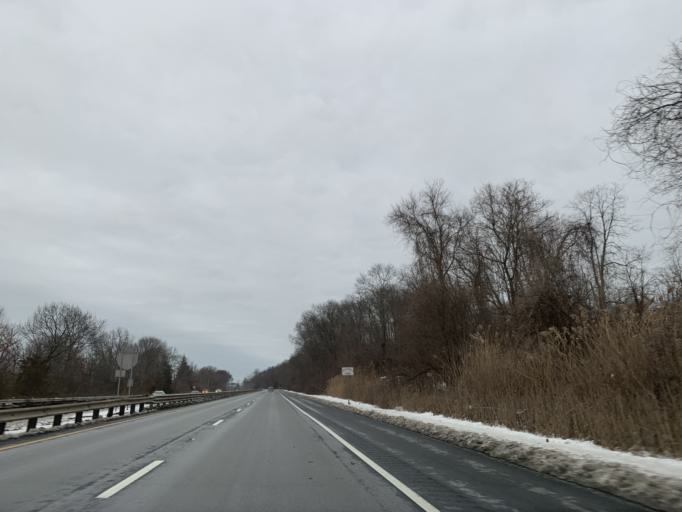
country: US
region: Massachusetts
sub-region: Bristol County
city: Somerset
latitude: 41.7327
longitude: -71.1339
